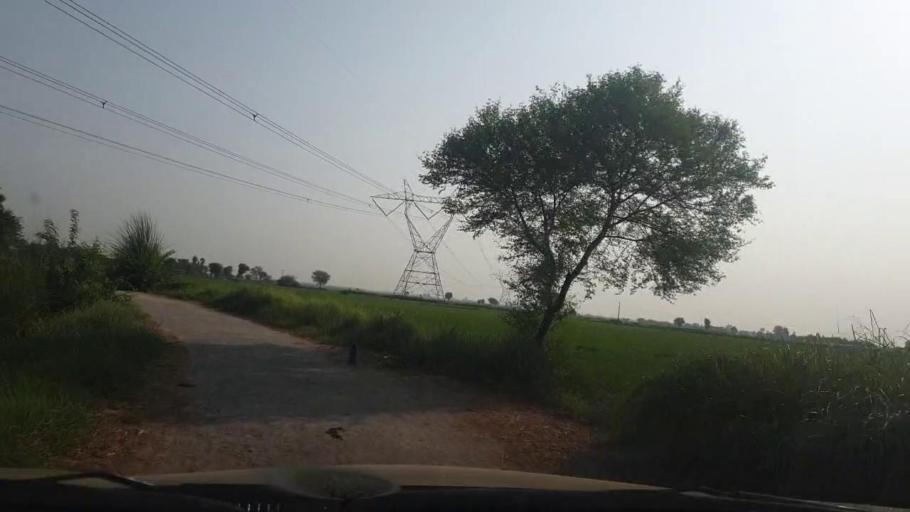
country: PK
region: Sindh
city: Larkana
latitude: 27.5916
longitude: 68.1606
